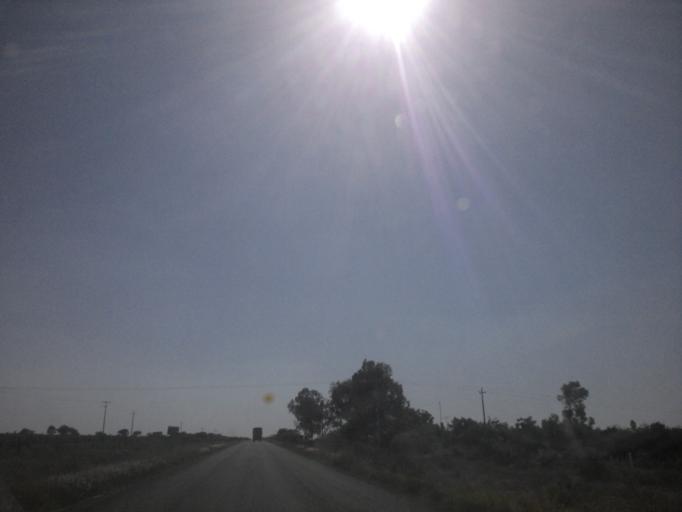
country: MX
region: Jalisco
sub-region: Arandas
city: Santiaguito (Santiaguito de Velazquez)
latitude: 20.8241
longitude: -102.1729
